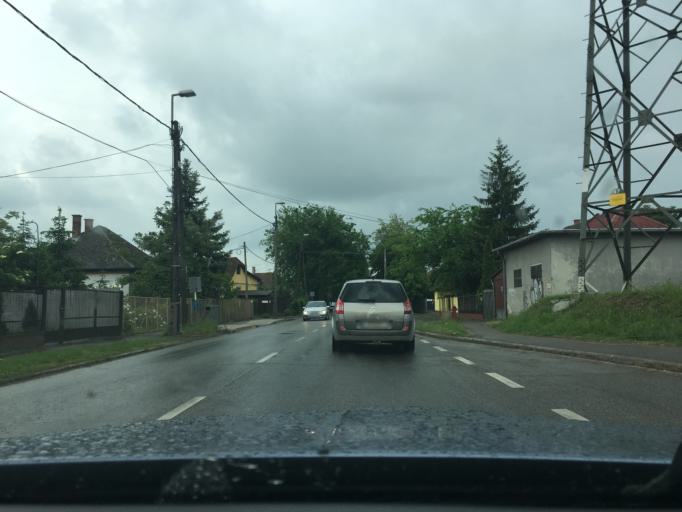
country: HU
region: Hajdu-Bihar
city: Debrecen
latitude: 47.5251
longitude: 21.6598
